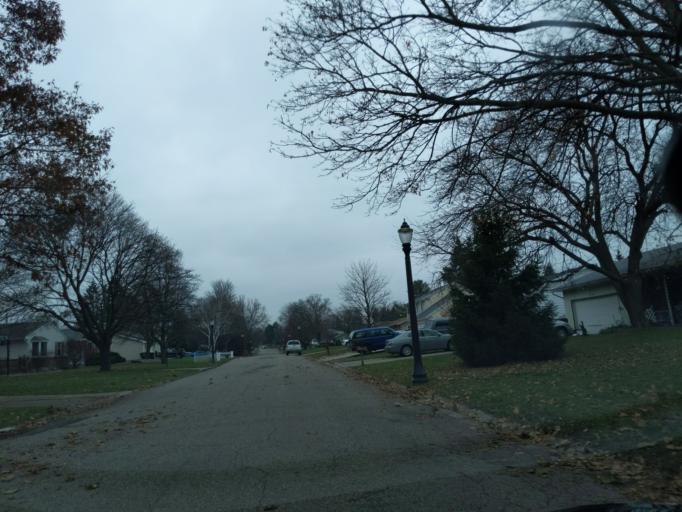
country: US
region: Michigan
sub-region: Eaton County
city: Waverly
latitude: 42.7298
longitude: -84.6318
